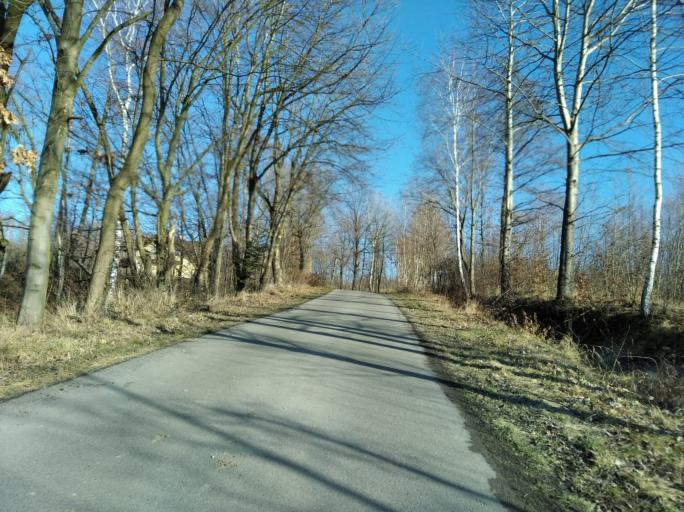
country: PL
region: Subcarpathian Voivodeship
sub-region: Powiat strzyzowski
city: Konieczkowa
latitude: 49.8579
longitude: 21.9354
